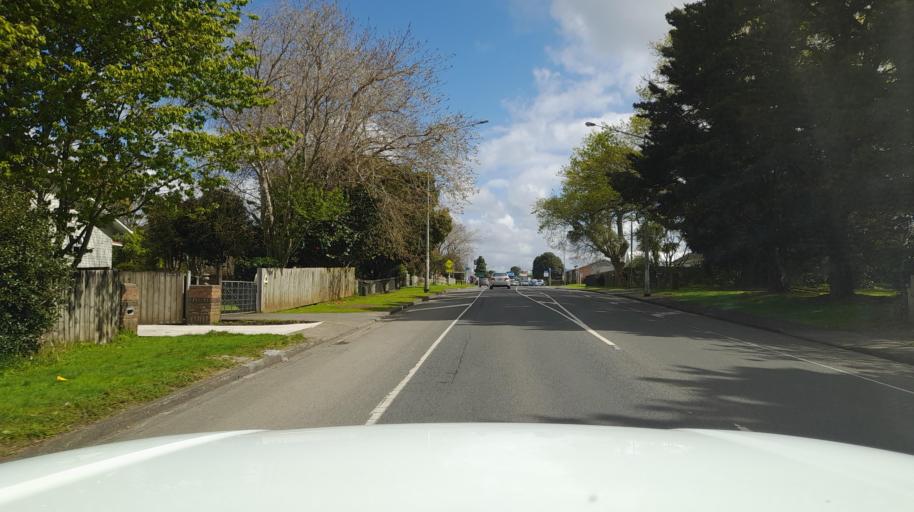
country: NZ
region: Northland
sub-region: Far North District
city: Waimate North
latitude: -35.4043
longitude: 173.8064
